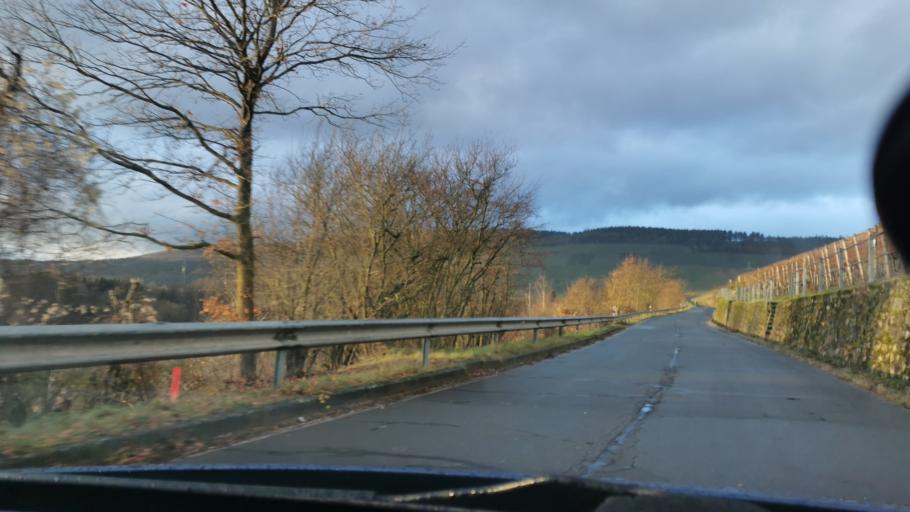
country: DE
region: Rheinland-Pfalz
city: Maring-Noviand
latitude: 49.9300
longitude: 7.0001
